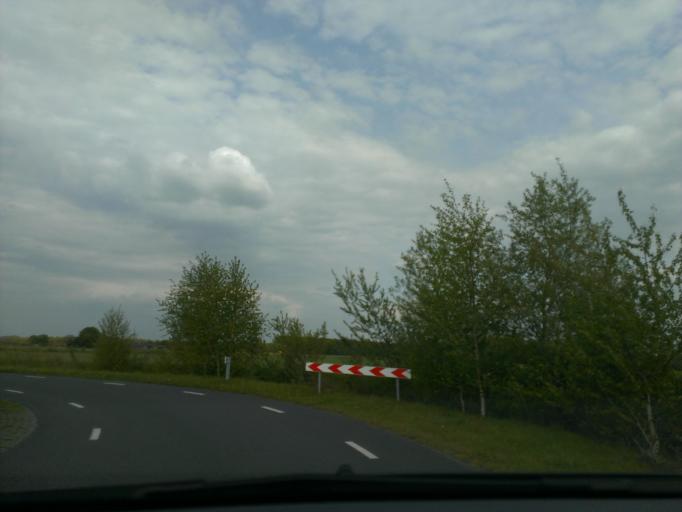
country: NL
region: Gelderland
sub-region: Gemeente Voorst
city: Twello
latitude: 52.2425
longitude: 6.0623
